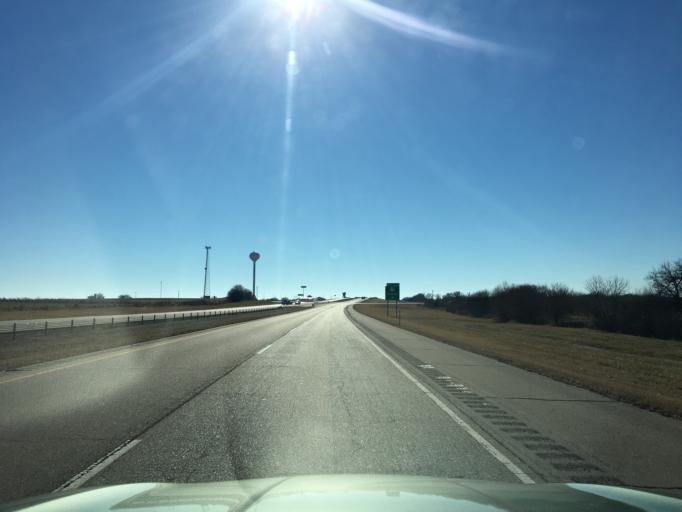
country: US
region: Oklahoma
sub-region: Kay County
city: Blackwell
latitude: 36.9477
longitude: -97.3458
